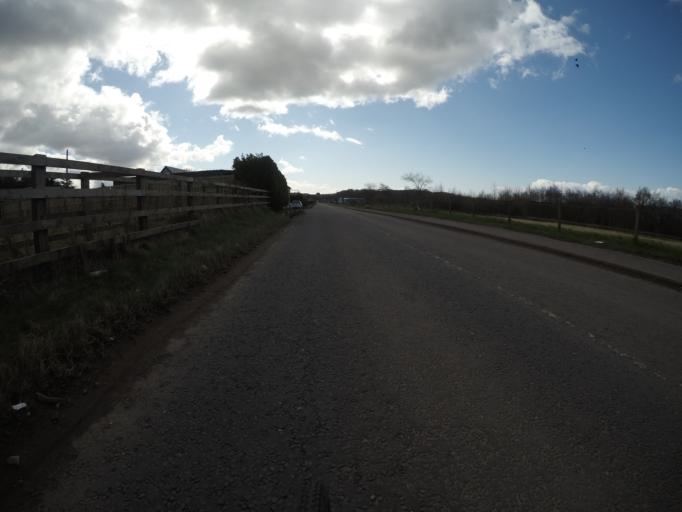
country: GB
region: Scotland
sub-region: North Ayrshire
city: Dreghorn
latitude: 55.5898
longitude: -4.6017
